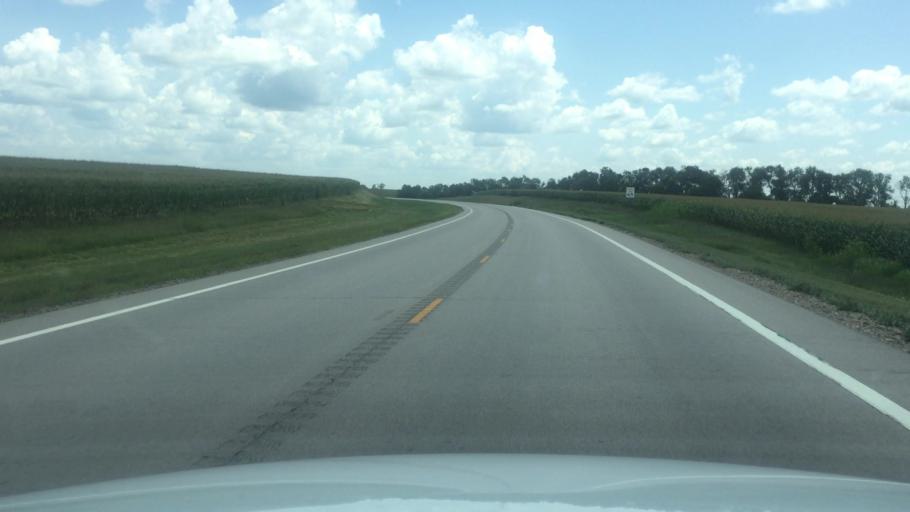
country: US
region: Kansas
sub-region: Brown County
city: Horton
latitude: 39.6624
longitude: -95.4132
